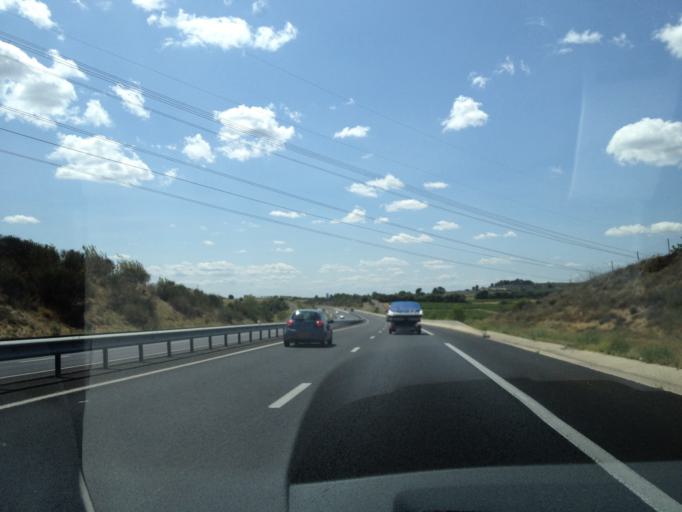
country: FR
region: Languedoc-Roussillon
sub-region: Departement de l'Herault
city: Paulhan
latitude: 43.5530
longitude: 3.4554
